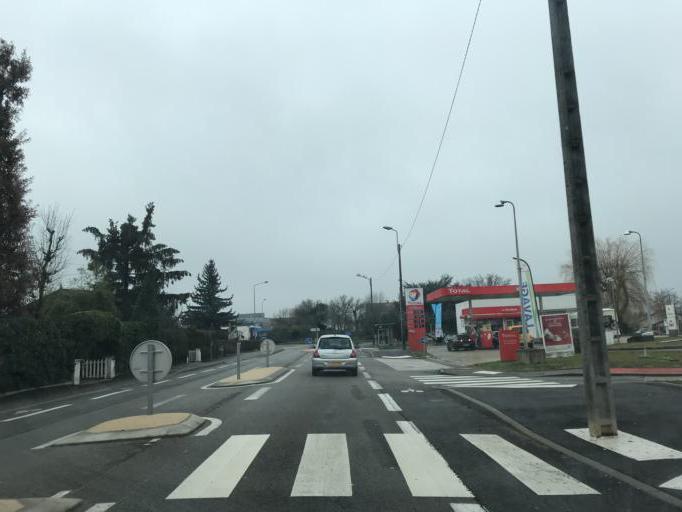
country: FR
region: Rhone-Alpes
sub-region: Departement de l'Ain
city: Saint-Denis-les-Bourg
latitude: 46.2009
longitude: 5.2001
